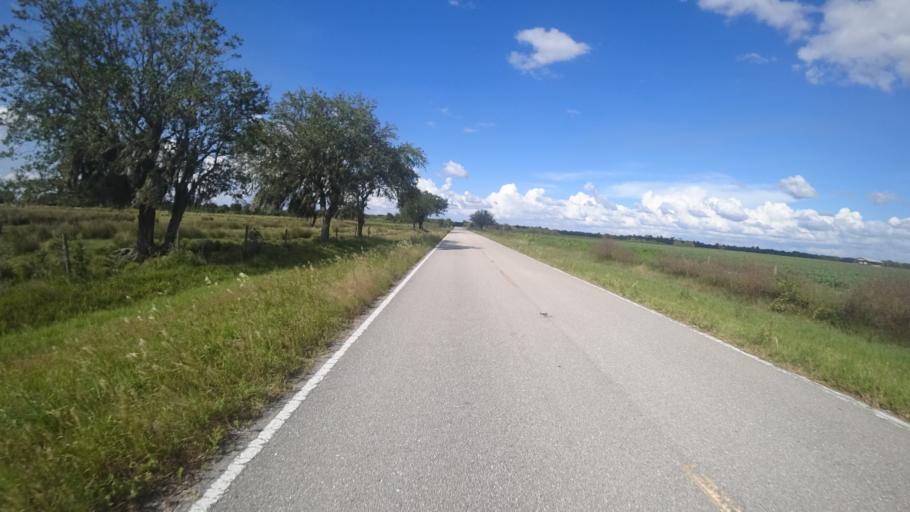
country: US
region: Florida
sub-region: DeSoto County
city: Arcadia
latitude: 27.2827
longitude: -82.0563
